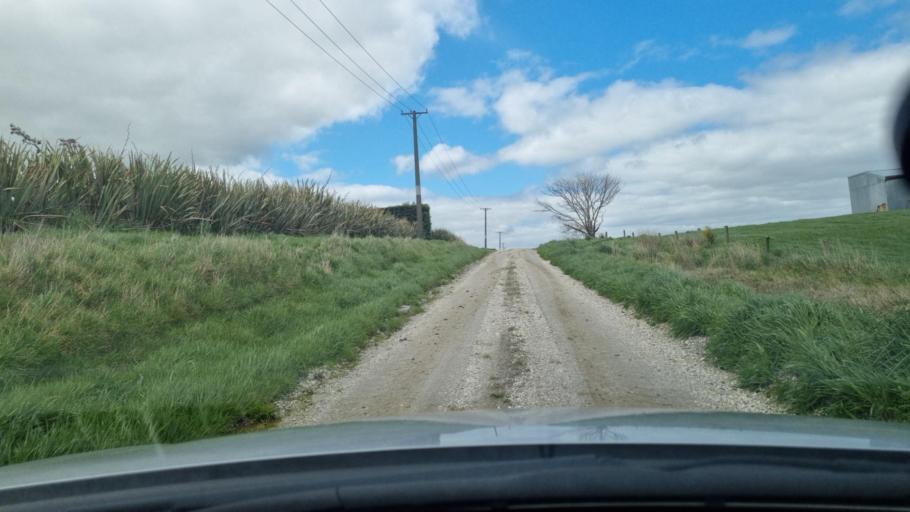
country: NZ
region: Southland
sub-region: Invercargill City
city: Invercargill
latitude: -46.4427
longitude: 168.4526
